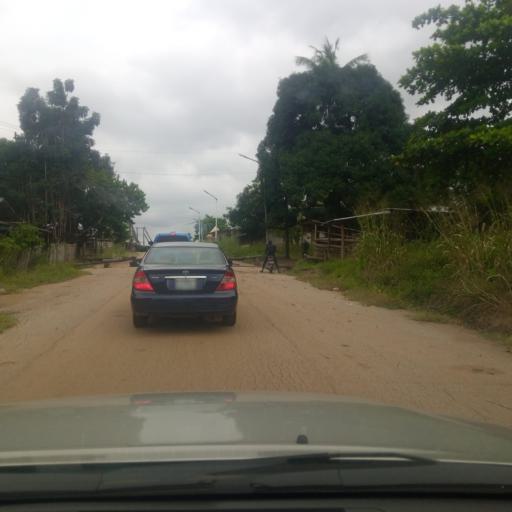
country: NG
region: Ebonyi
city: Effium
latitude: 6.6283
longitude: 8.0546
